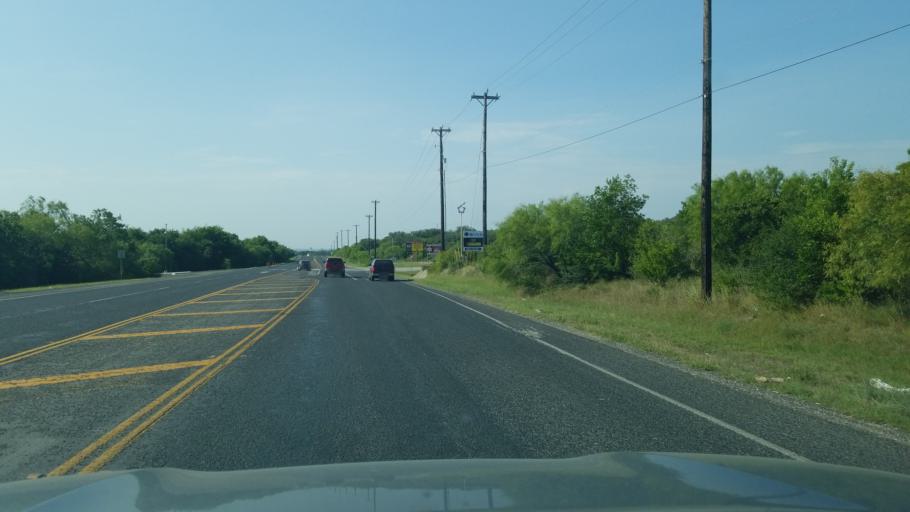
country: US
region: Texas
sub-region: Medina County
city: La Coste
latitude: 29.4127
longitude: -98.7810
